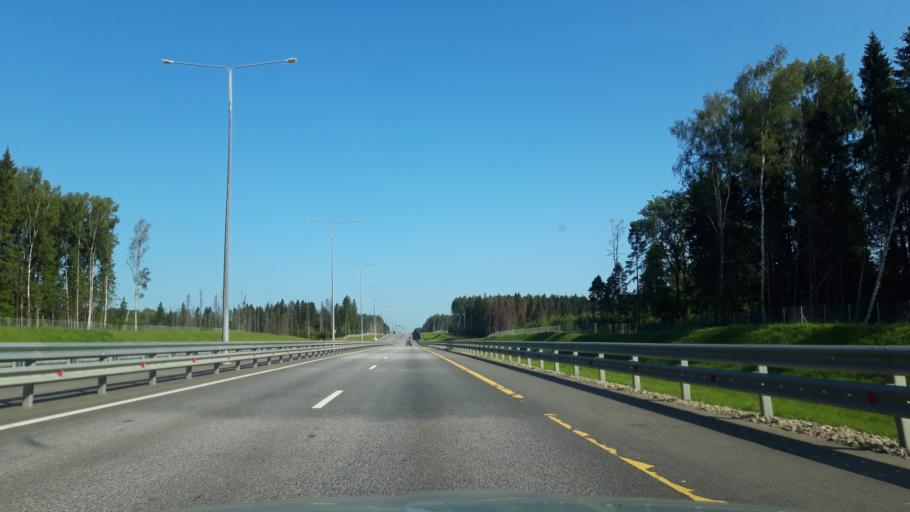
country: RU
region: Moskovskaya
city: Klin
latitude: 56.2571
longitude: 36.7354
